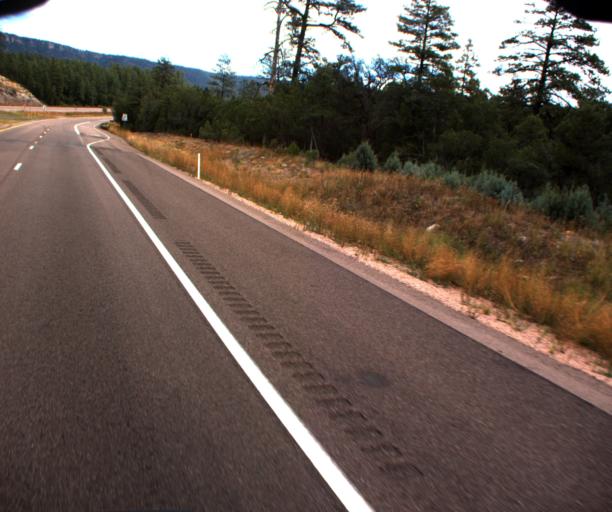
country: US
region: Arizona
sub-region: Gila County
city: Star Valley
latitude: 34.3119
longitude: -111.0410
